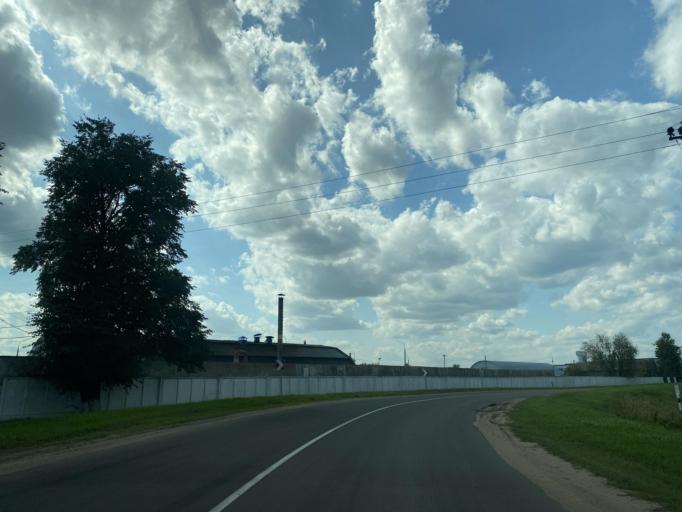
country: BY
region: Minsk
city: Horad Zhodzina
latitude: 54.0862
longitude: 28.3625
